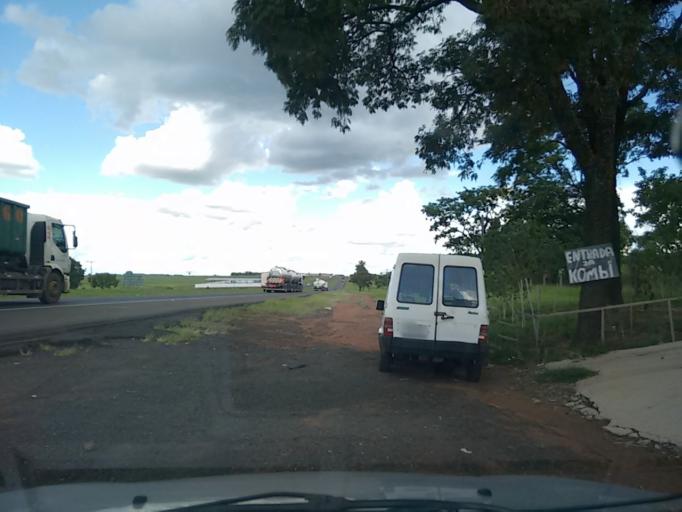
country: BR
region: Sao Paulo
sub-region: Ibate
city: Ibate
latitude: -21.9227
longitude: -48.0318
